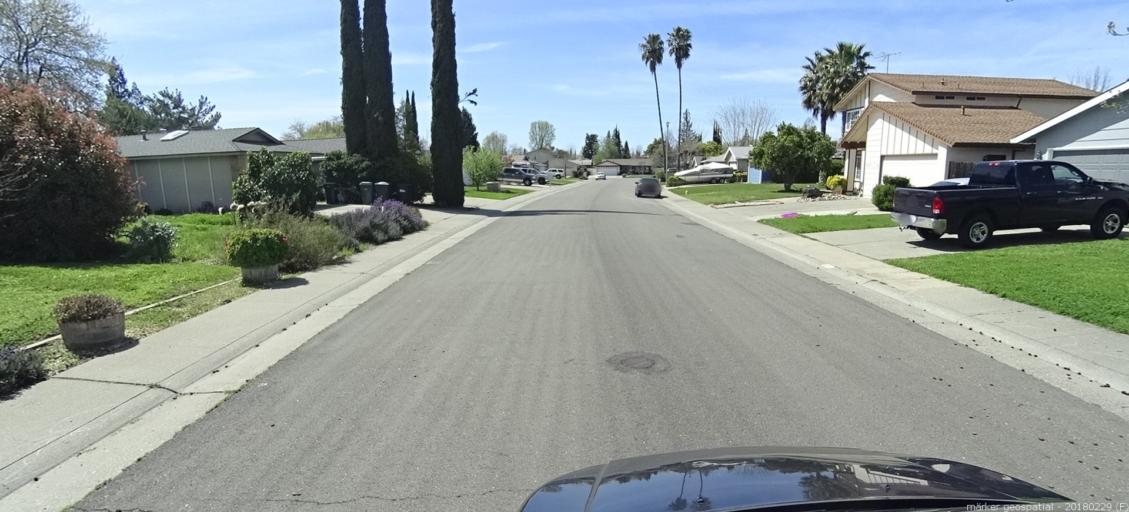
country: US
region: California
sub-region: Sacramento County
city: Rosemont
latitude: 38.5535
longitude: -121.3504
